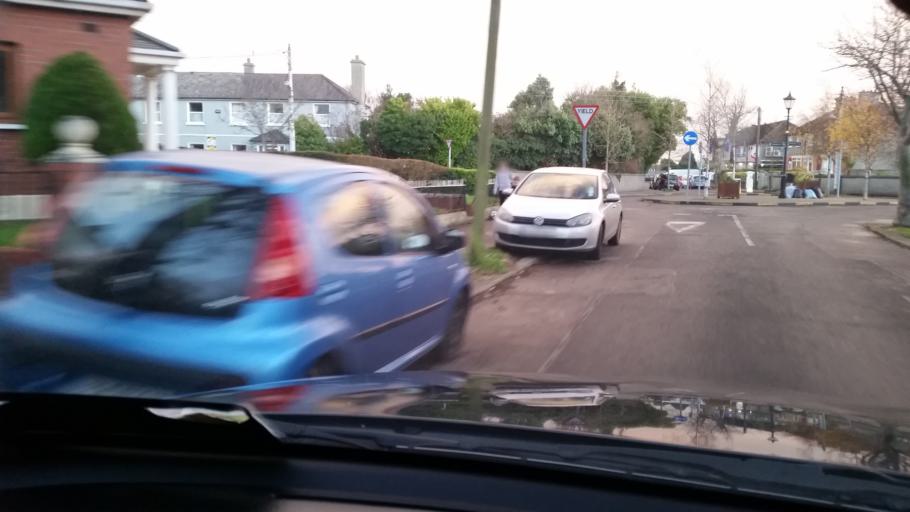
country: IE
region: Leinster
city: Beaumont
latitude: 53.3816
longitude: -6.2474
